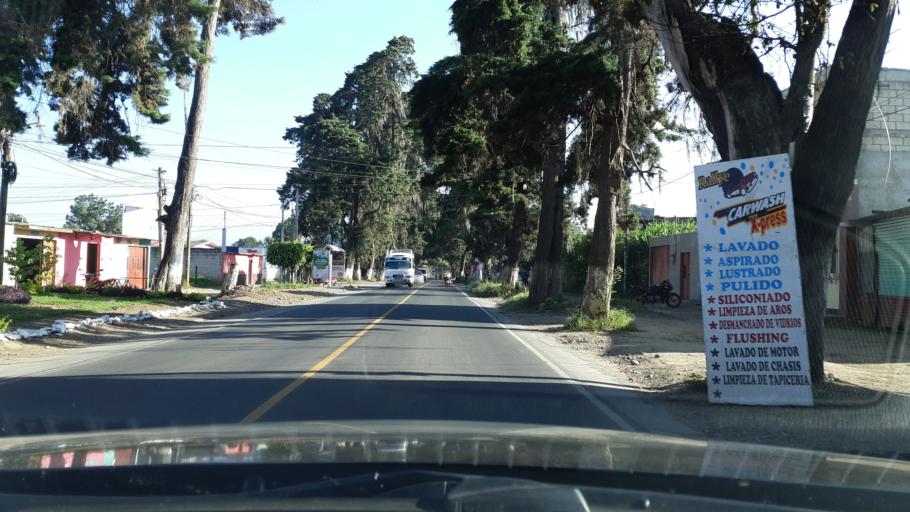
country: GT
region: Chimaltenango
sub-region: Municipio de Chimaltenango
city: Chimaltenango
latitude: 14.6472
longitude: -90.8125
